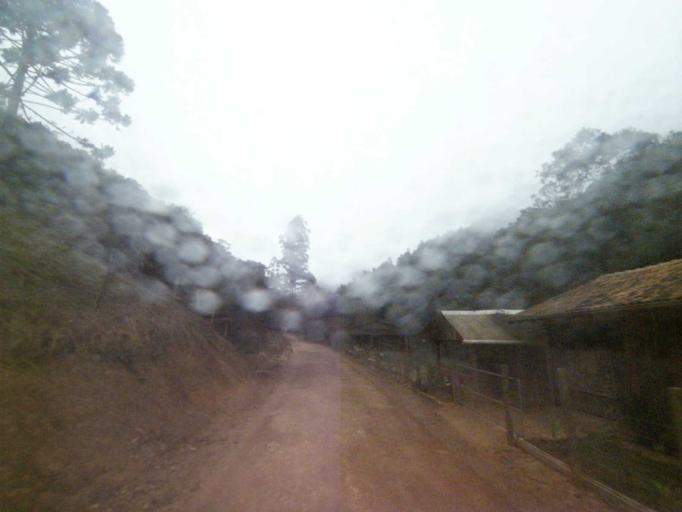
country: BR
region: Santa Catarina
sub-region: Anitapolis
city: Anitapolis
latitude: -27.8665
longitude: -49.1317
